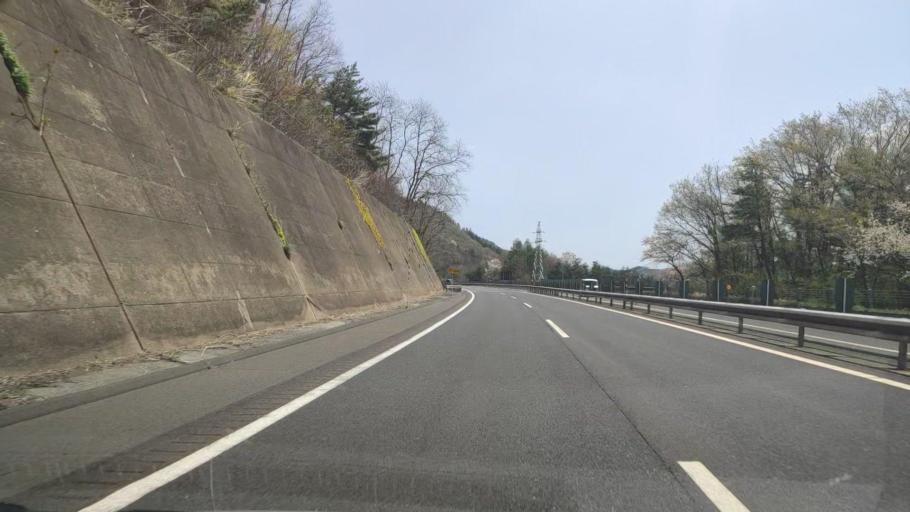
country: JP
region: Iwate
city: Ichinohe
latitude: 40.2316
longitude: 141.3057
